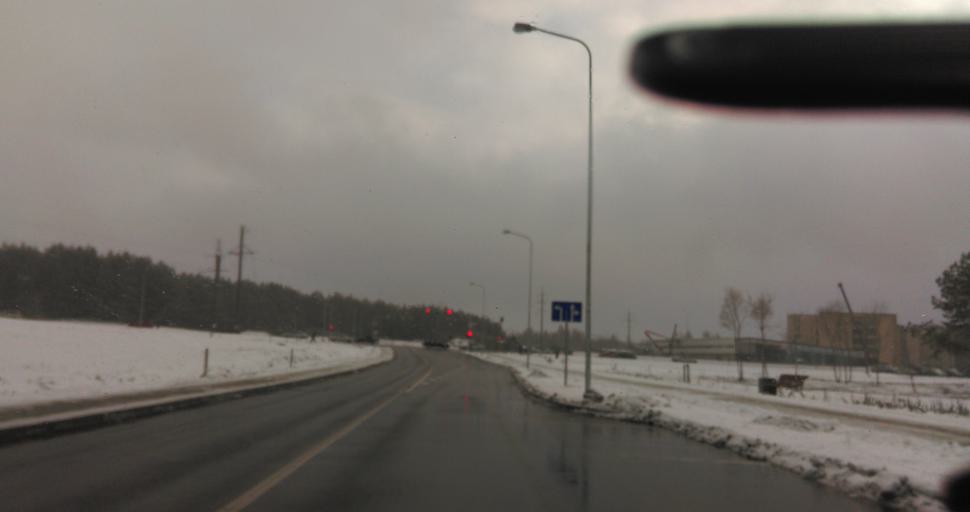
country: LT
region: Utenos apskritis
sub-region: Utena
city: Utena
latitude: 55.5044
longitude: 25.6180
